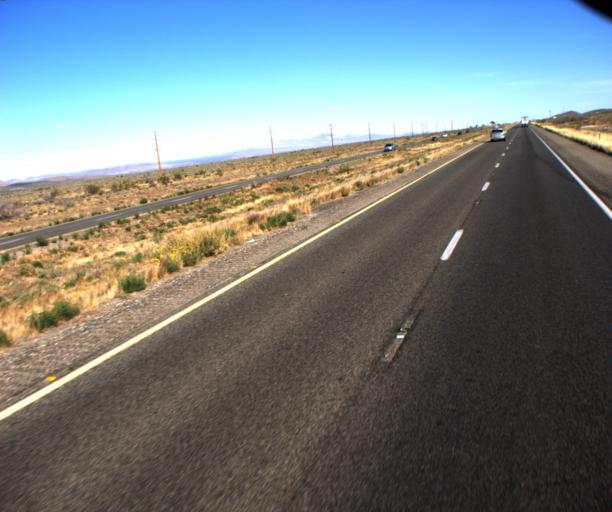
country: US
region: Arizona
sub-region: Mohave County
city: Golden Valley
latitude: 35.3862
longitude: -114.2514
